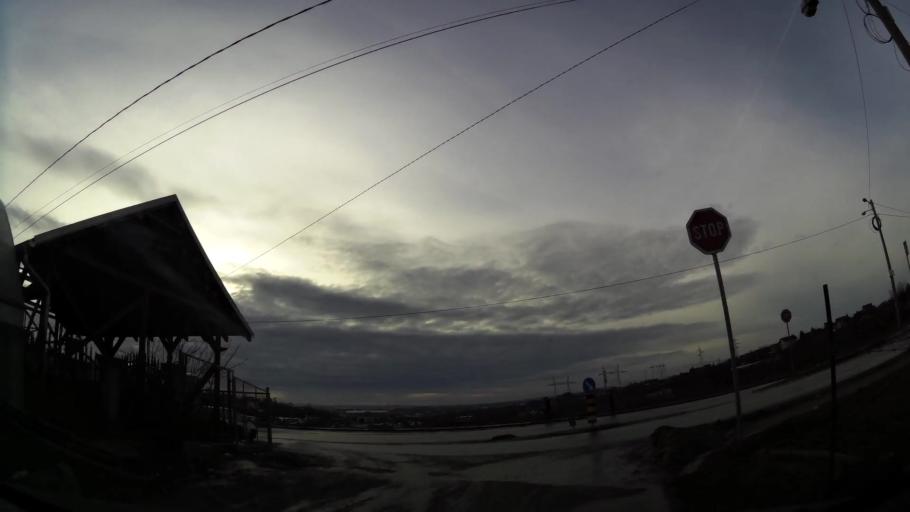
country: RS
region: Central Serbia
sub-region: Belgrade
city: Zvezdara
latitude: 44.7189
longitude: 20.5044
